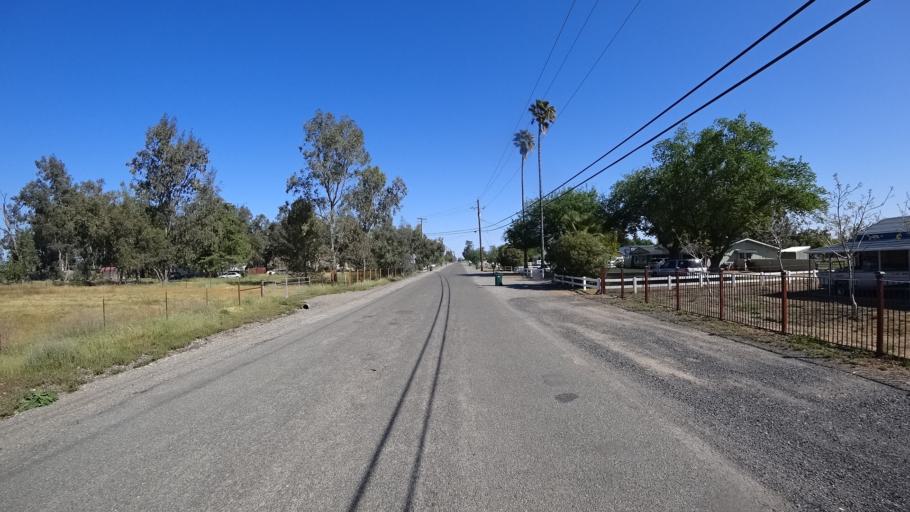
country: US
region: California
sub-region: Glenn County
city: Orland
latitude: 39.7263
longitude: -122.1689
